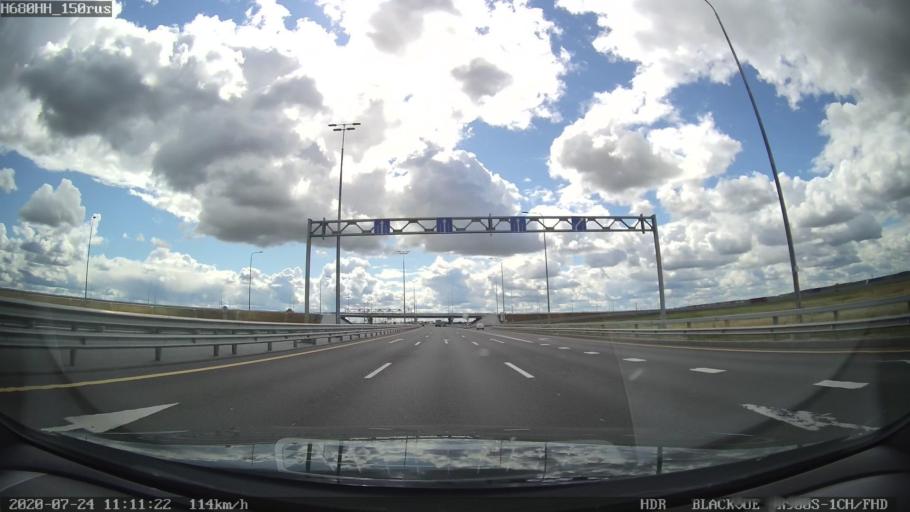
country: RU
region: St.-Petersburg
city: Tyarlevo
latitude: 59.7238
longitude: 30.5144
